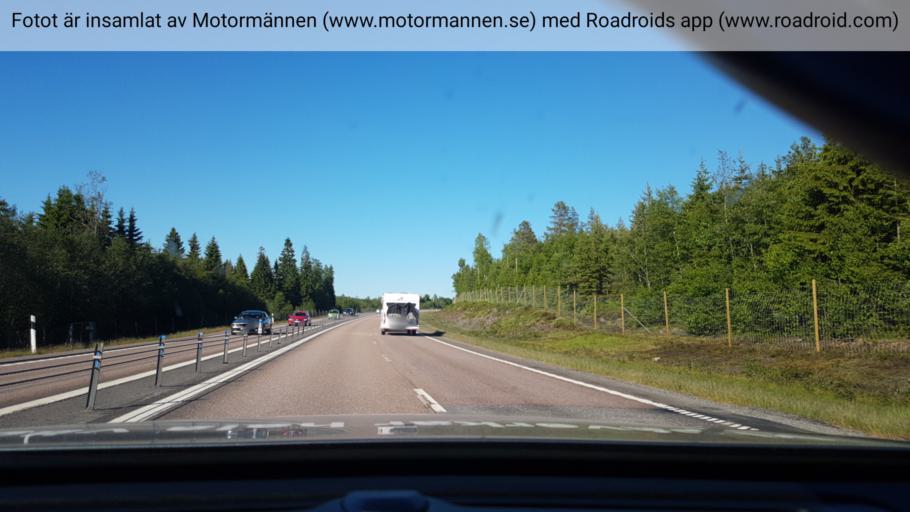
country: SE
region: Vaesternorrland
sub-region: Haernoesands Kommun
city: Haernoesand
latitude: 62.6050
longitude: 17.8196
